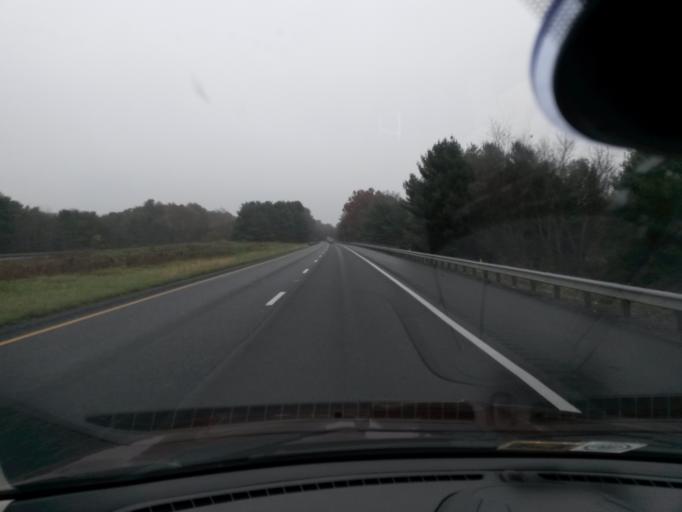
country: US
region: Virginia
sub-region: Carroll County
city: Woodlawn
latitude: 36.7768
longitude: -80.8185
